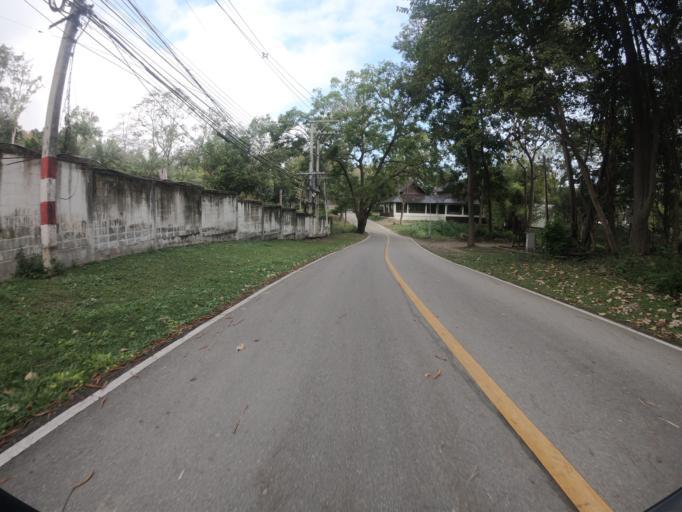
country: TH
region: Chiang Mai
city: Chiang Mai
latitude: 18.8062
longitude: 98.9474
